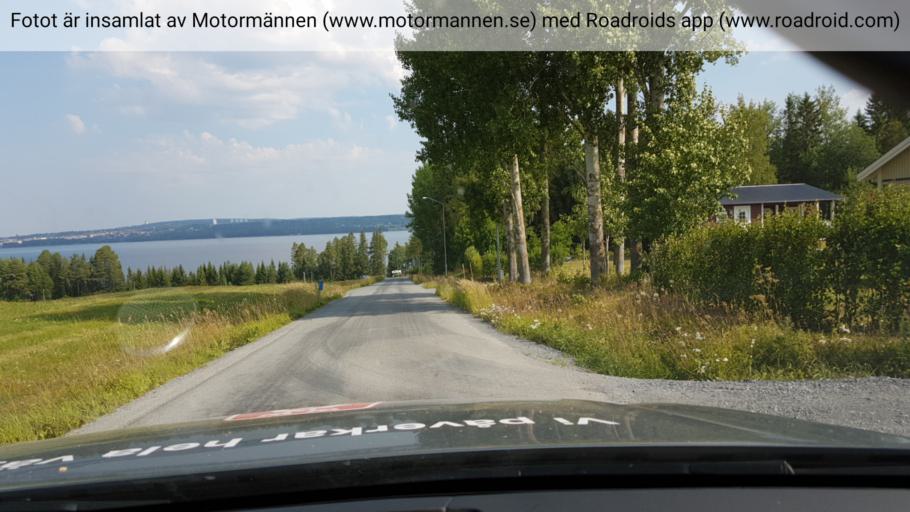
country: SE
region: Jaemtland
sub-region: OEstersunds Kommun
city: Ostersund
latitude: 63.1297
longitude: 14.6588
